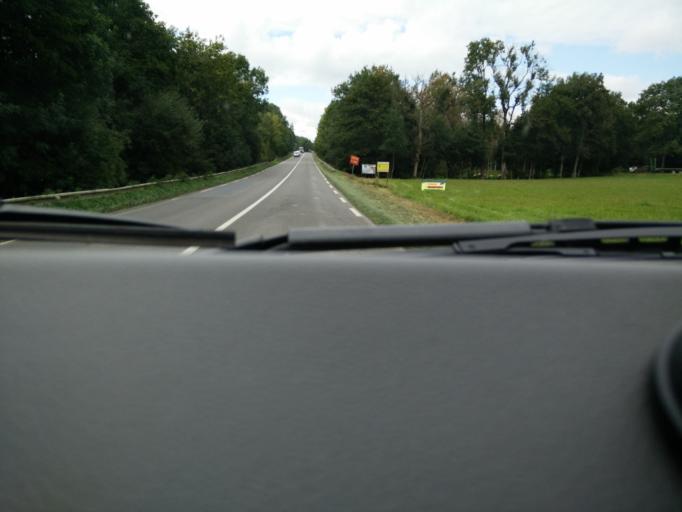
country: FR
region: Champagne-Ardenne
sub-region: Departement des Ardennes
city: Renwez
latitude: 49.8129
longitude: 4.6084
